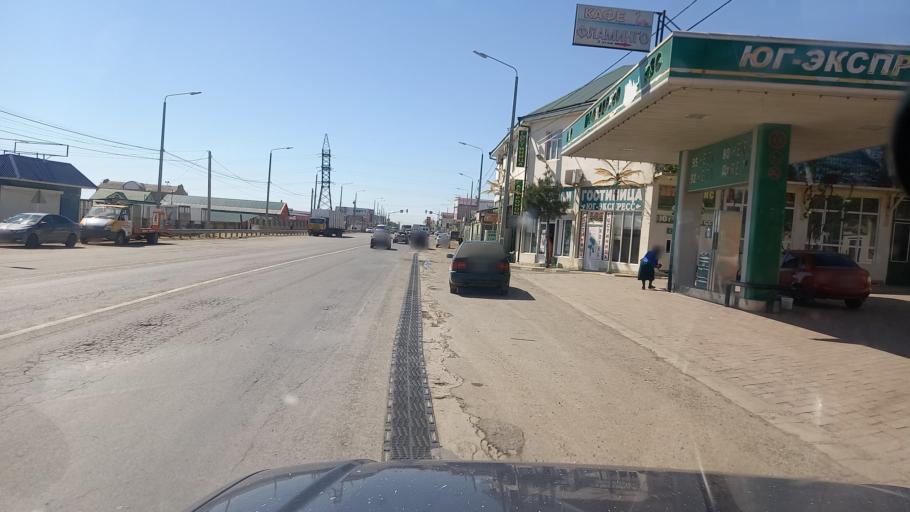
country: RU
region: Dagestan
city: Derbent
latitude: 42.0349
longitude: 48.2944
